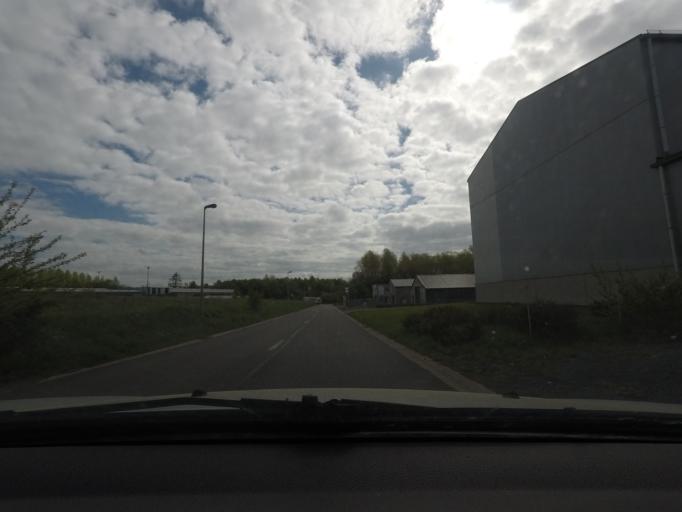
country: BE
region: Wallonia
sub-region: Province du Luxembourg
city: Habay-la-Vieille
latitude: 49.7026
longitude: 5.6275
